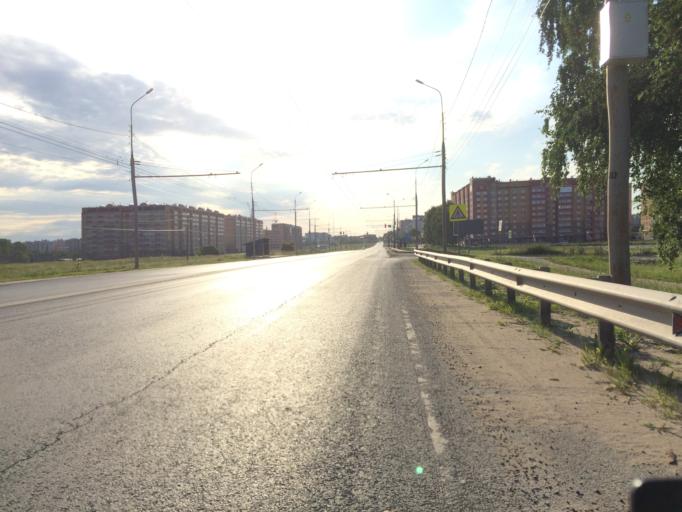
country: RU
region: Mariy-El
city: Medvedevo
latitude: 56.6395
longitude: 47.8142
